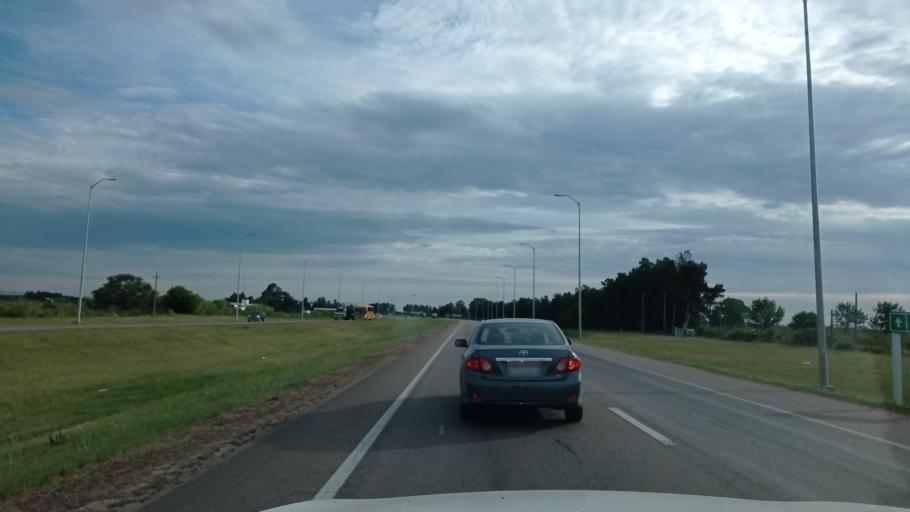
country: UY
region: Canelones
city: La Paz
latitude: -34.7769
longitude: -56.2730
